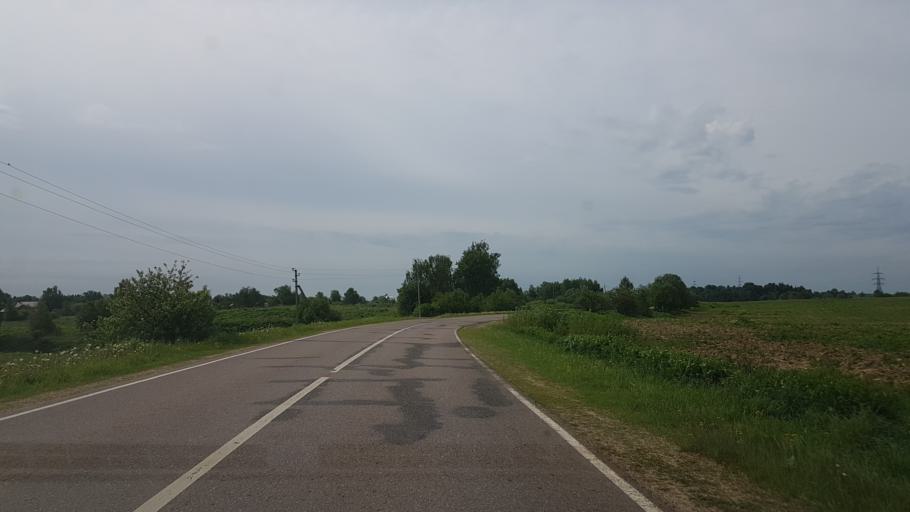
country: RU
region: Moskovskaya
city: Klin
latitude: 56.1274
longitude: 36.7522
